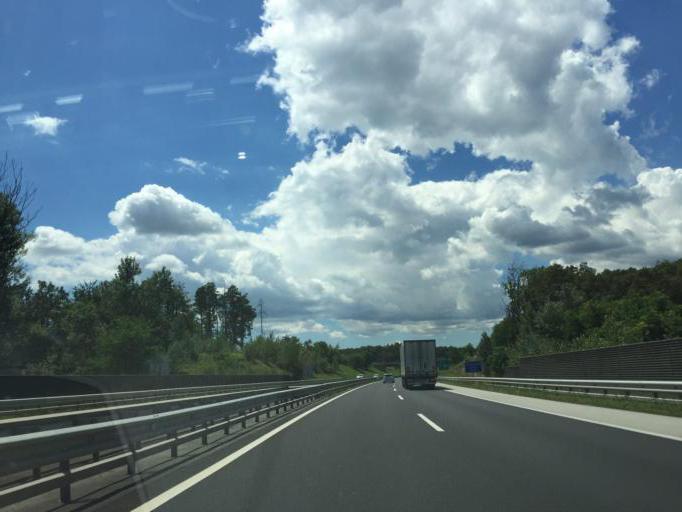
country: SI
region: Miklavz na Dravskem Polju
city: Miklavz na Dravskem Polju
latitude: 46.5272
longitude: 15.6971
